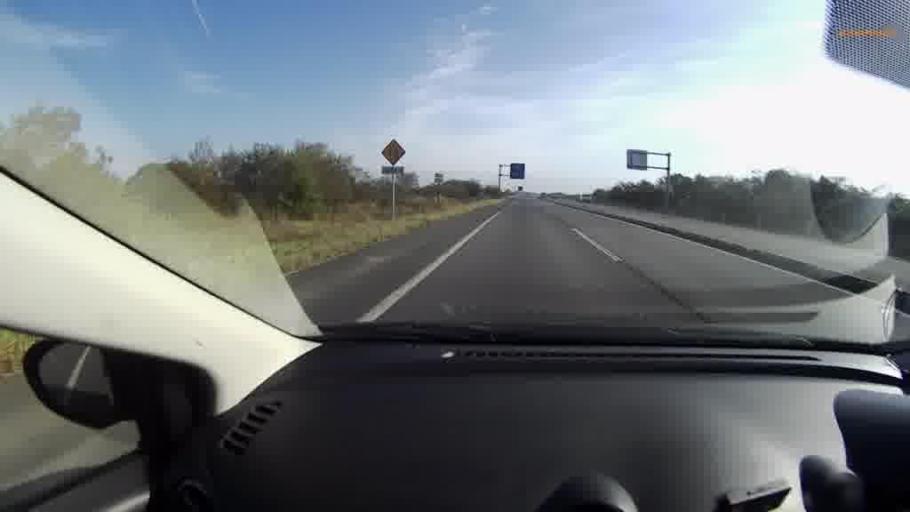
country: JP
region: Hokkaido
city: Kushiro
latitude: 43.0317
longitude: 144.3053
